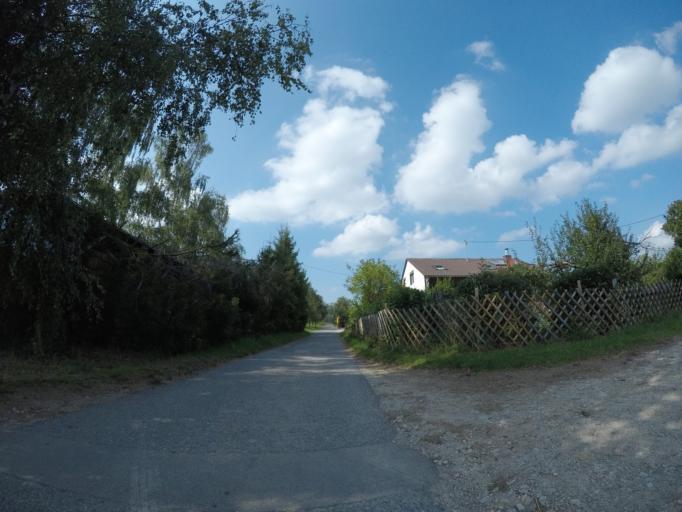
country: DE
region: Baden-Wuerttemberg
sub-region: Tuebingen Region
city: Pfullingen
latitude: 48.4528
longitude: 9.1939
